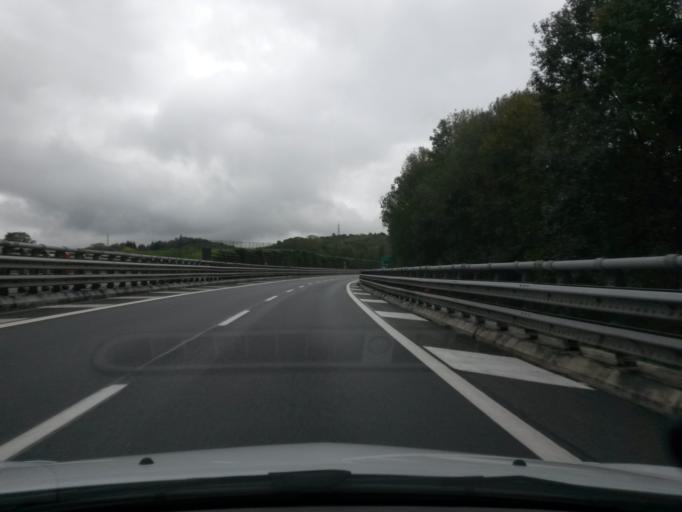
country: IT
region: Piedmont
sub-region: Provincia di Torino
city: Caselette
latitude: 45.0875
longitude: 7.4856
